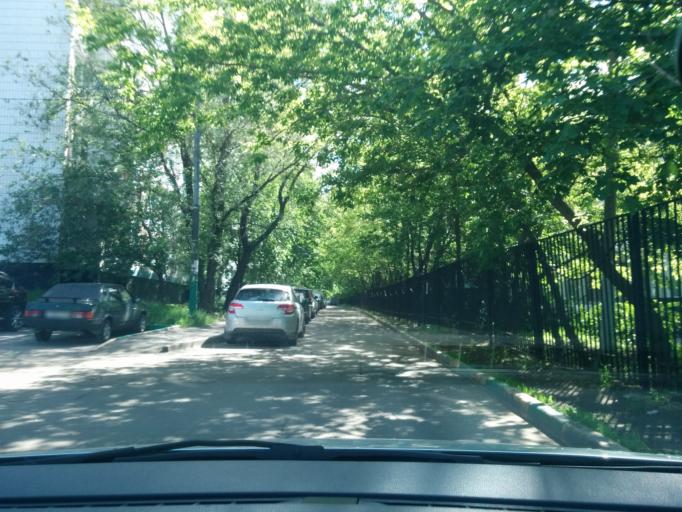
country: RU
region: Moskovskaya
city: Izmaylovo
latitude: 55.7922
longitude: 37.8111
